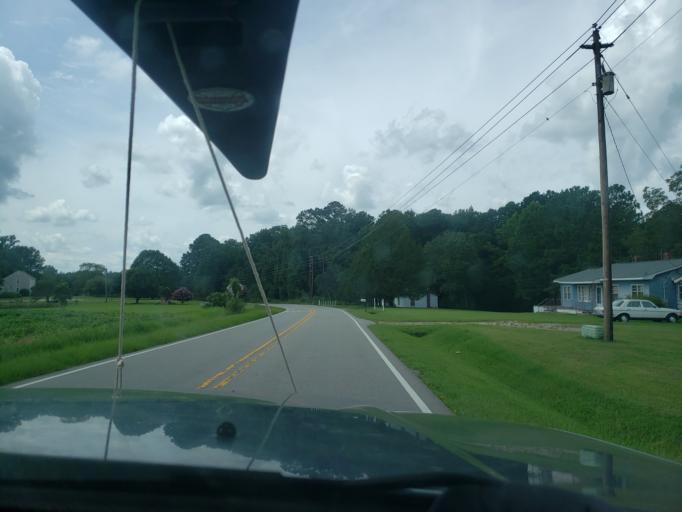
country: US
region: North Carolina
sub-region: Wake County
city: Zebulon
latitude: 35.8820
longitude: -78.3691
